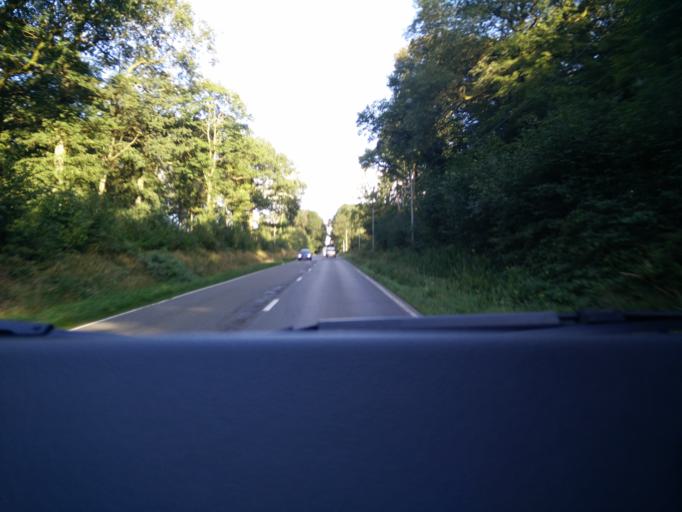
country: BE
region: Wallonia
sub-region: Province de Namur
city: Philippeville
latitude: 50.2041
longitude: 4.4851
